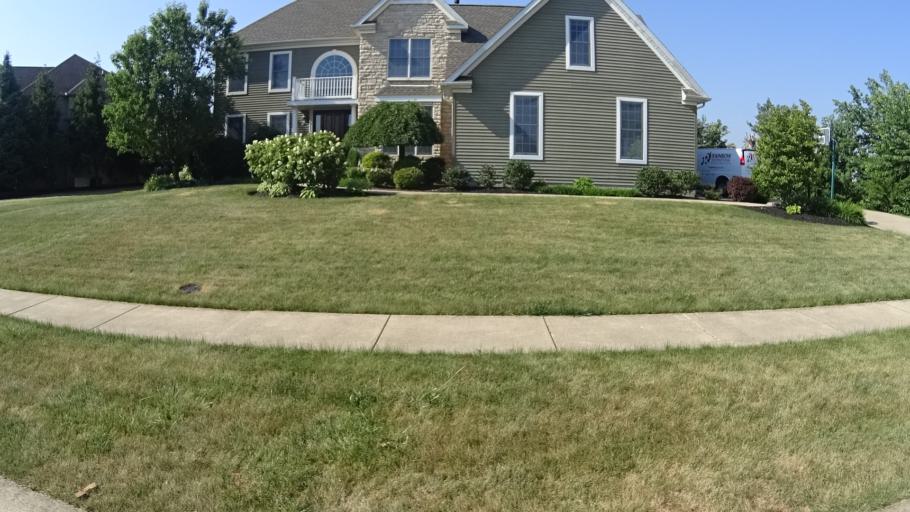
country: US
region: Ohio
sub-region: Erie County
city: Huron
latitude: 41.4058
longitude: -82.5750
